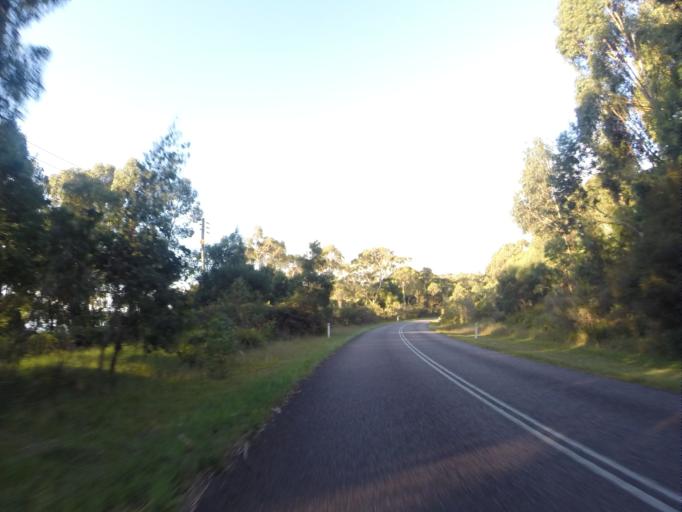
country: AU
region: New South Wales
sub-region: Shoalhaven Shire
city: Kangaroo Valley
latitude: -34.6477
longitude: 150.5058
